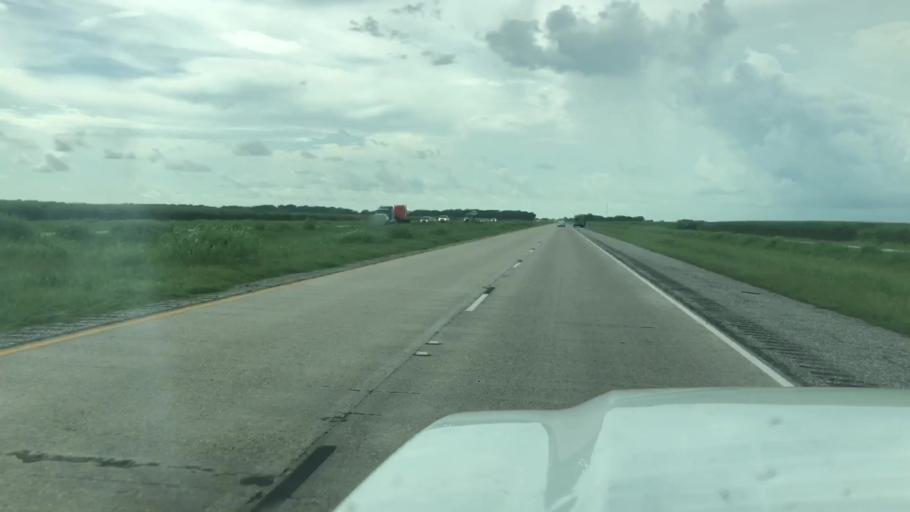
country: US
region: Louisiana
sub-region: Saint Mary Parish
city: Baldwin
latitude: 29.8488
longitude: -91.5931
